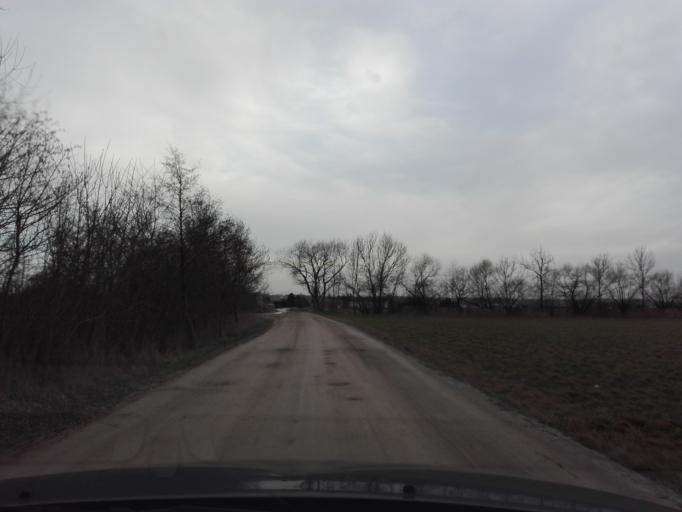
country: AT
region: Upper Austria
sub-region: Politischer Bezirk Linz-Land
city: Horsching
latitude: 48.2117
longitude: 14.1542
